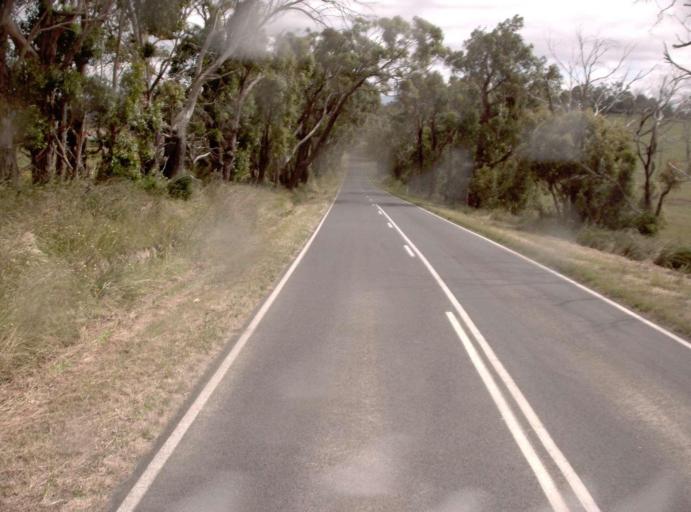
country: AU
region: Victoria
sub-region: Latrobe
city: Moe
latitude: -38.1414
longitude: 146.1472
